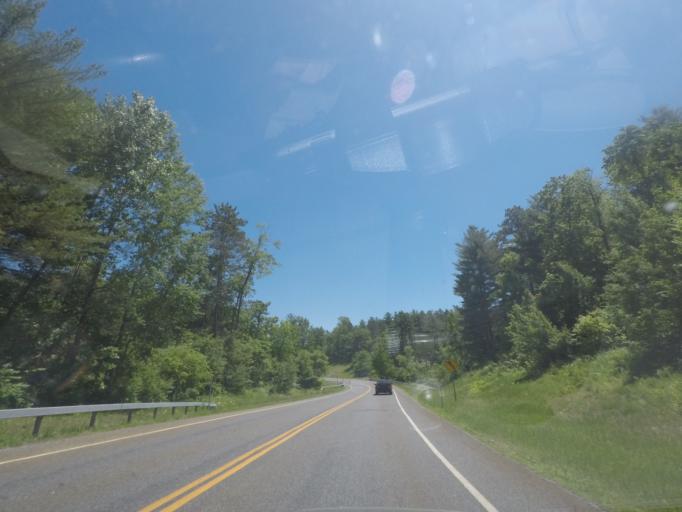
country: US
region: New York
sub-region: Saratoga County
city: Mechanicville
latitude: 42.9468
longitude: -73.7292
